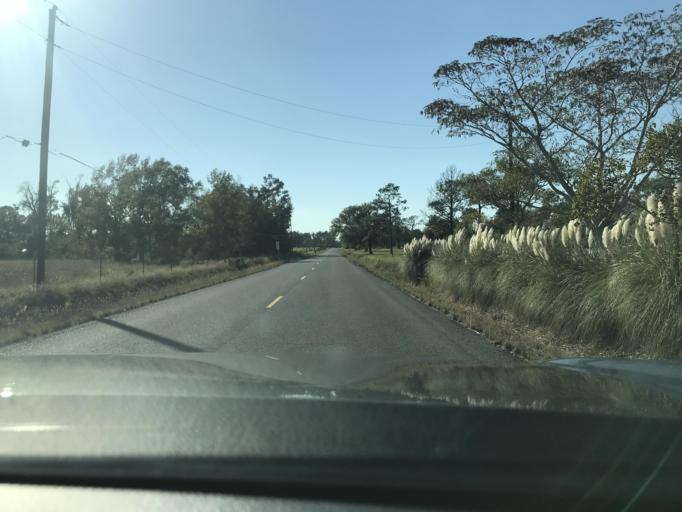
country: US
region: Louisiana
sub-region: Calcasieu Parish
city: Westlake
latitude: 30.3153
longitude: -93.2641
